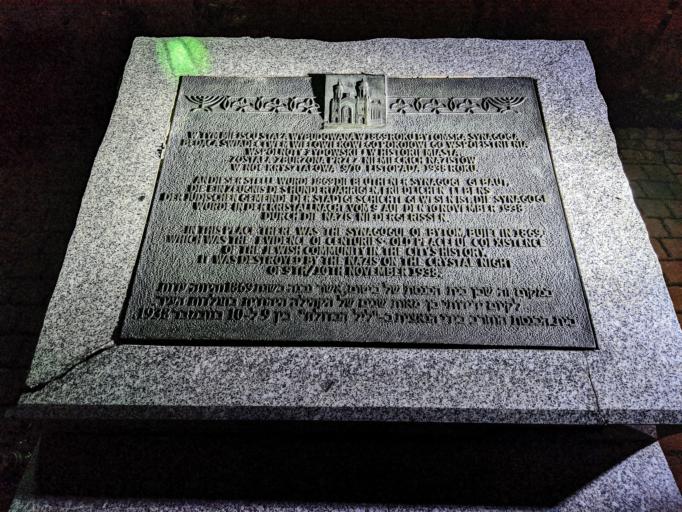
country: PL
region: Silesian Voivodeship
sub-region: Bytom
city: Bytom
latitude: 50.3478
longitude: 18.9250
